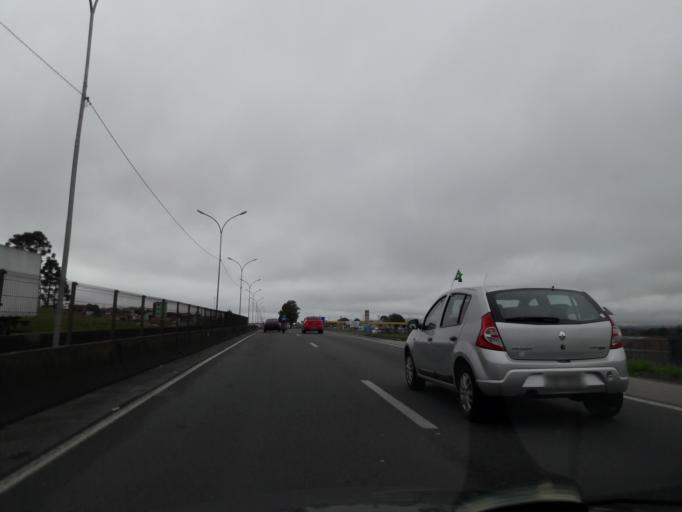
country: BR
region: Parana
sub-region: Quatro Barras
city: Quatro Barras
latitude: -25.3692
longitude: -49.1125
